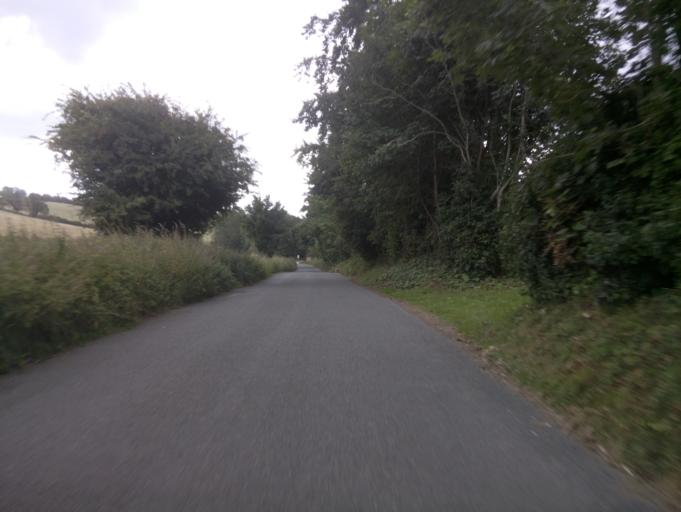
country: GB
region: England
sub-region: Gloucestershire
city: Shurdington
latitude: 51.7921
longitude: -2.1193
